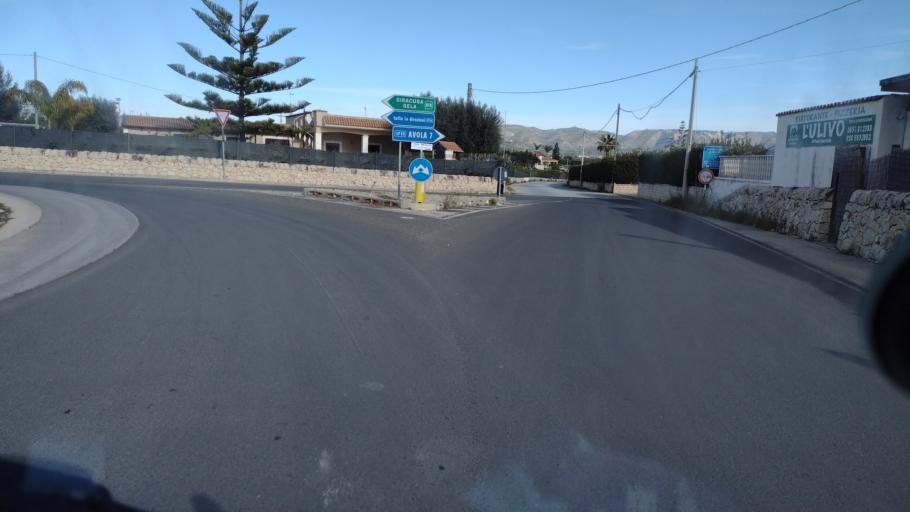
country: IT
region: Sicily
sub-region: Provincia di Siracusa
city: Avola
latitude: 36.8716
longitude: 15.1277
